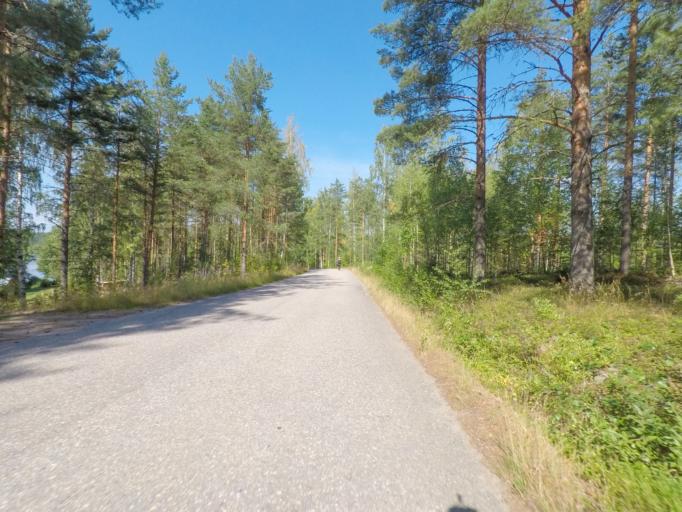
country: FI
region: Southern Savonia
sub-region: Mikkeli
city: Puumala
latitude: 61.4188
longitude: 28.0931
